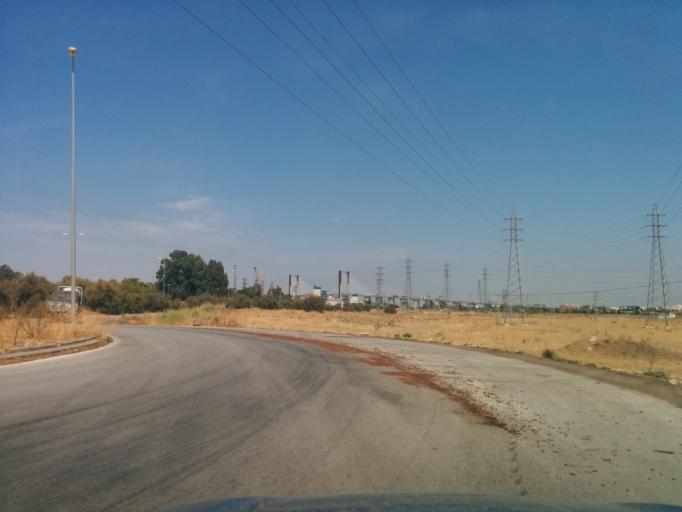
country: ES
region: Andalusia
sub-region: Provincia de Sevilla
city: Gelves
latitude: 37.3341
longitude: -5.9896
